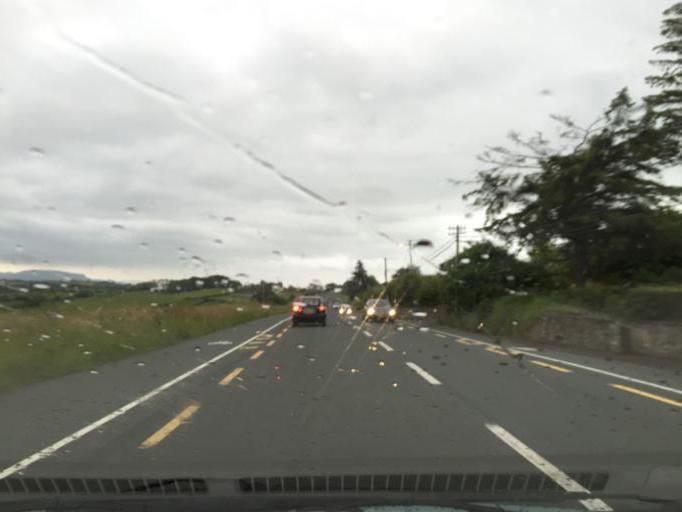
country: IE
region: Connaught
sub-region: Sligo
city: Strandhill
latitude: 54.2737
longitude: -8.5667
